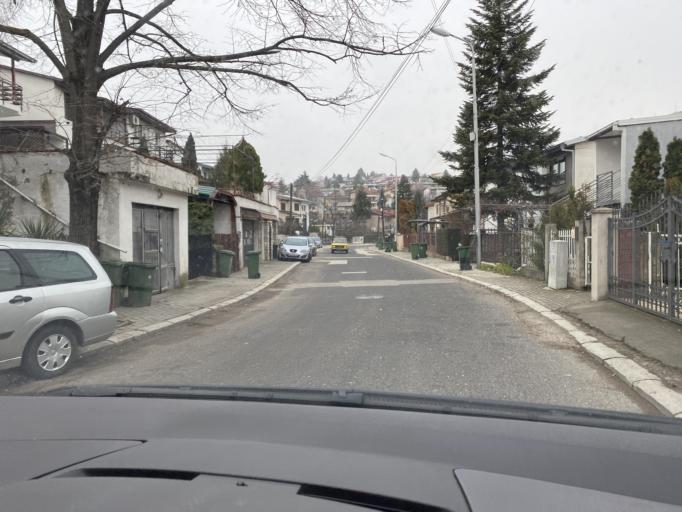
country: MK
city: Radishani
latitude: 42.0575
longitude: 21.4494
